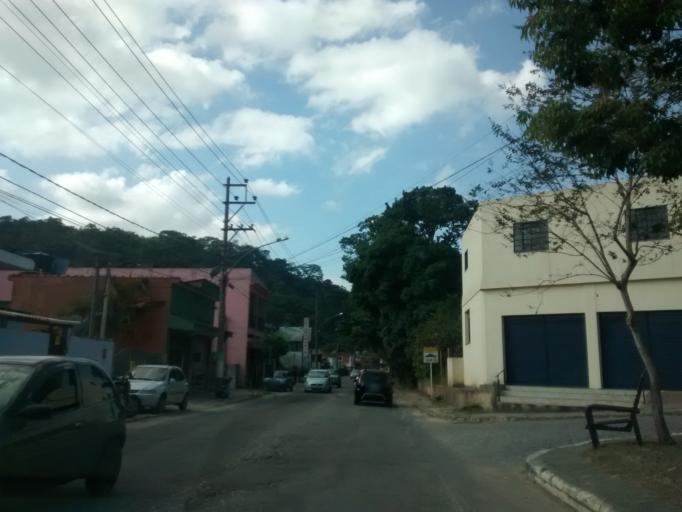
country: BR
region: Rio de Janeiro
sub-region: Miguel Pereira
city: Miguel Pereira
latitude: -22.4591
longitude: -43.4795
